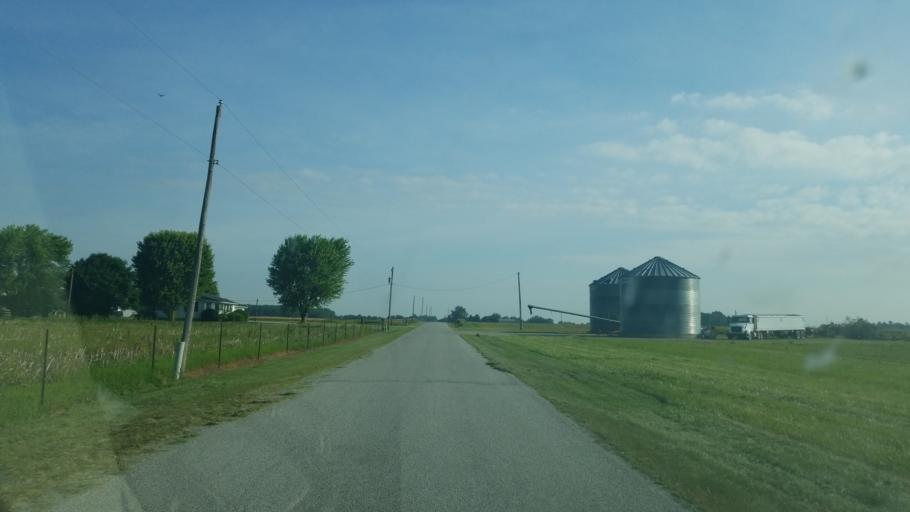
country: US
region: Ohio
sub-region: Hancock County
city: Arlington
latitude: 40.8078
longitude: -83.6706
